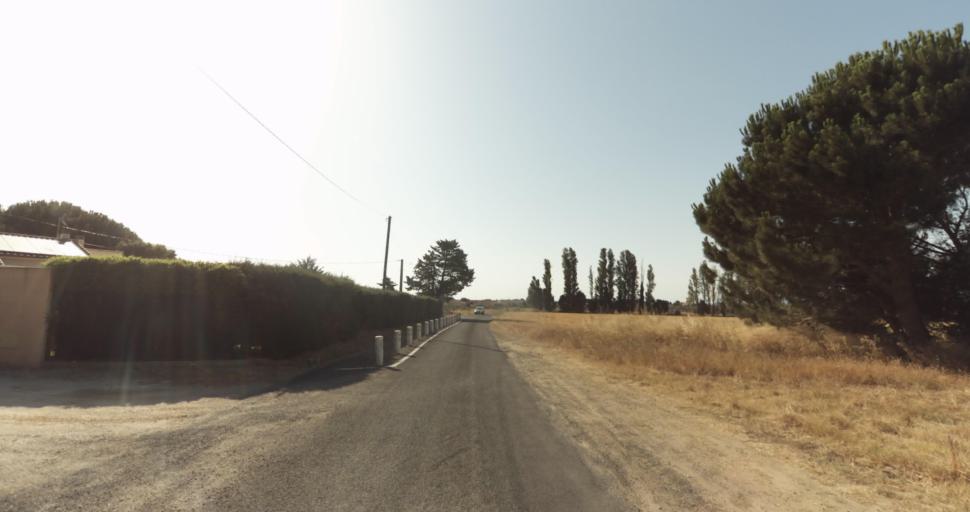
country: FR
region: Languedoc-Roussillon
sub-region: Departement des Pyrenees-Orientales
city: Alenya
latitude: 42.6453
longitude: 2.9730
